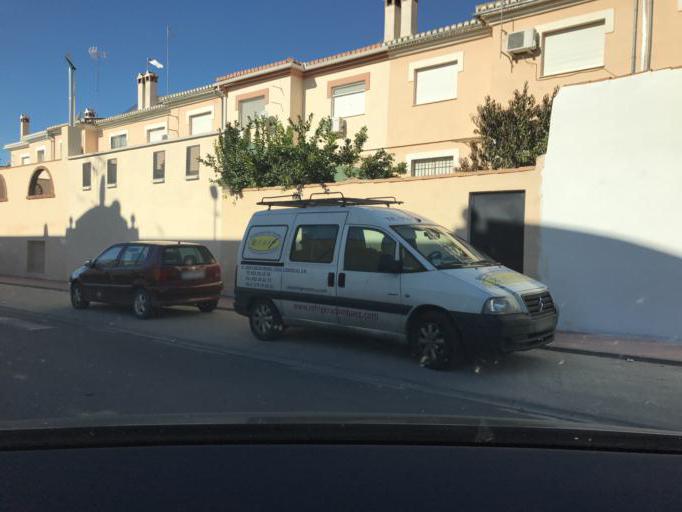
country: ES
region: Andalusia
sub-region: Provincia de Granada
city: Peligros
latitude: 37.2286
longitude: -3.6343
